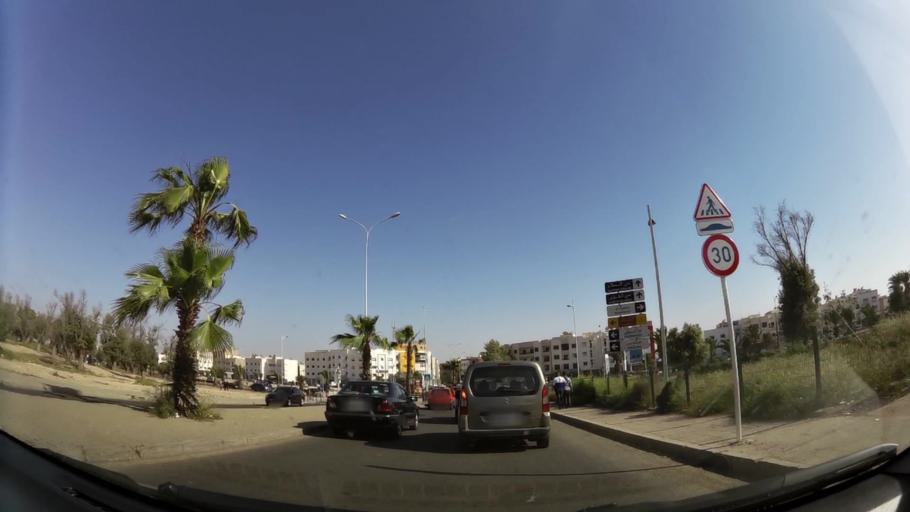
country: MA
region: Oued ed Dahab-Lagouira
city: Dakhla
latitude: 30.4048
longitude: -9.5510
